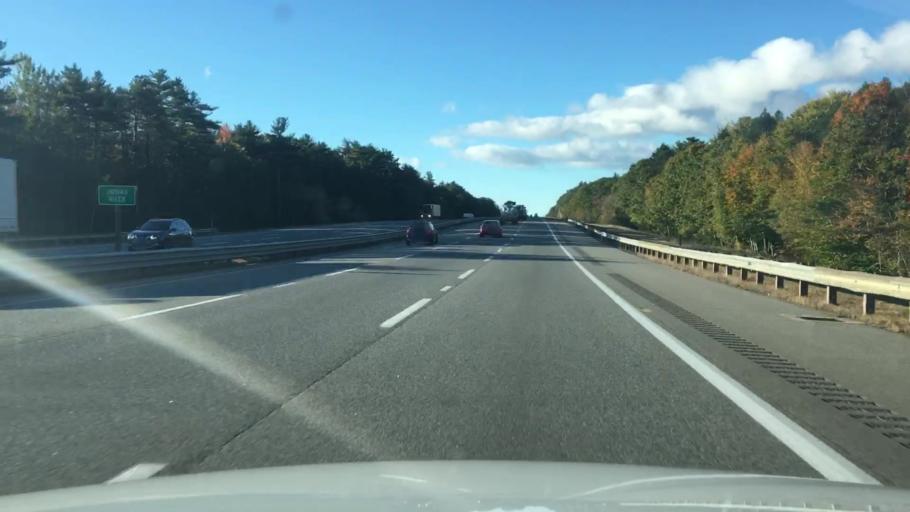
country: US
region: Maine
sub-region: York County
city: Cape Neddick
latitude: 43.2217
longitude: -70.6378
